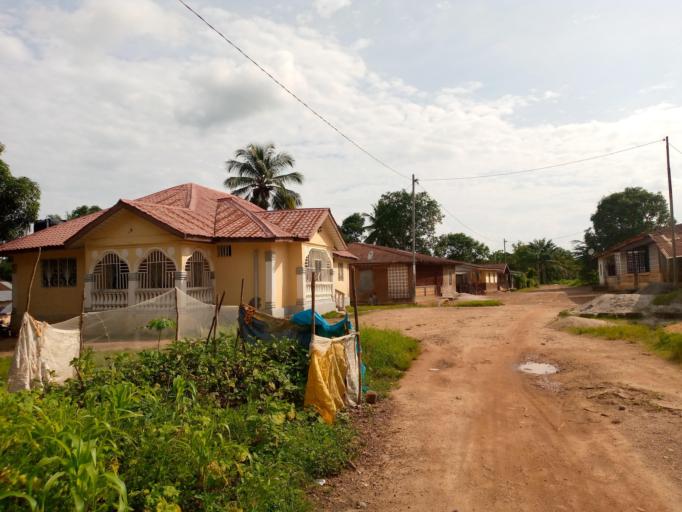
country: SL
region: Northern Province
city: Magburaka
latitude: 8.7218
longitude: -11.9495
